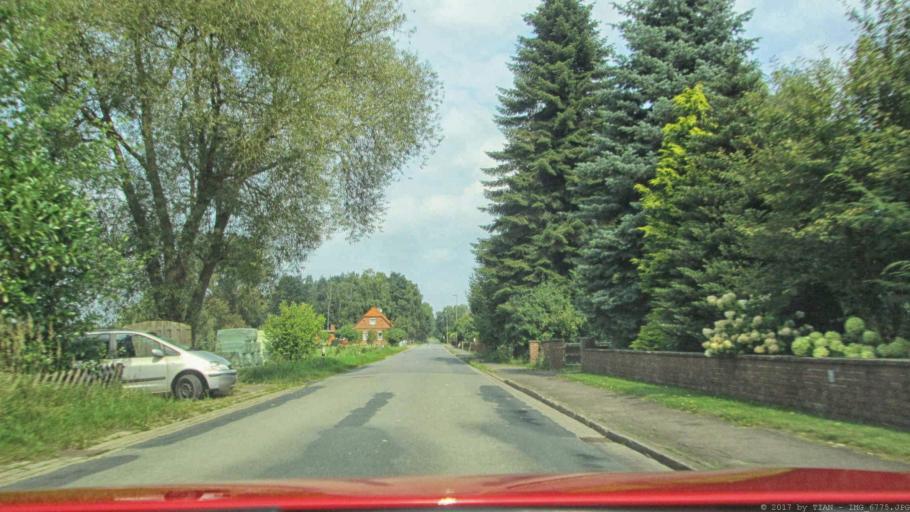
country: DE
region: Lower Saxony
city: Bad Bevensen
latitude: 53.0478
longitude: 10.6036
